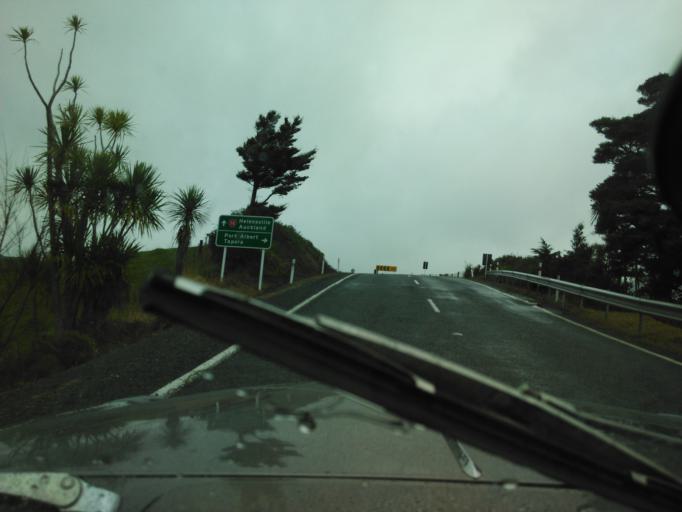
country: NZ
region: Auckland
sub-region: Auckland
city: Wellsford
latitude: -36.3662
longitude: 174.4518
